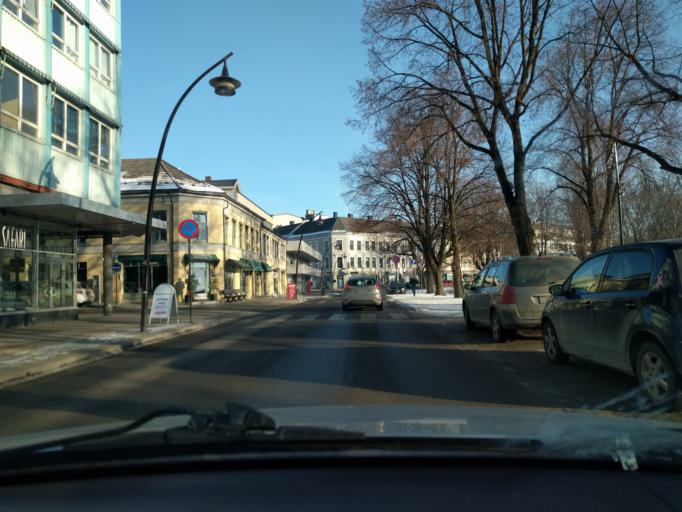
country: NO
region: Hedmark
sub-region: Hamar
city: Hamar
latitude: 60.7944
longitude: 11.0689
